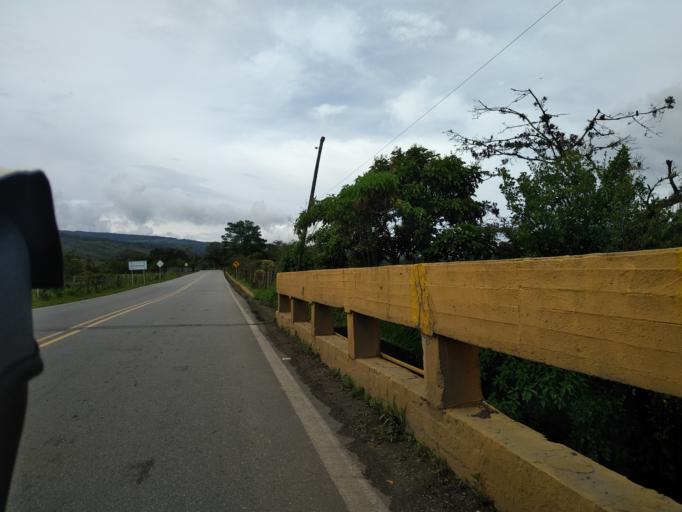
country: CO
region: Santander
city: Suaita
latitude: 6.1186
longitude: -73.3670
